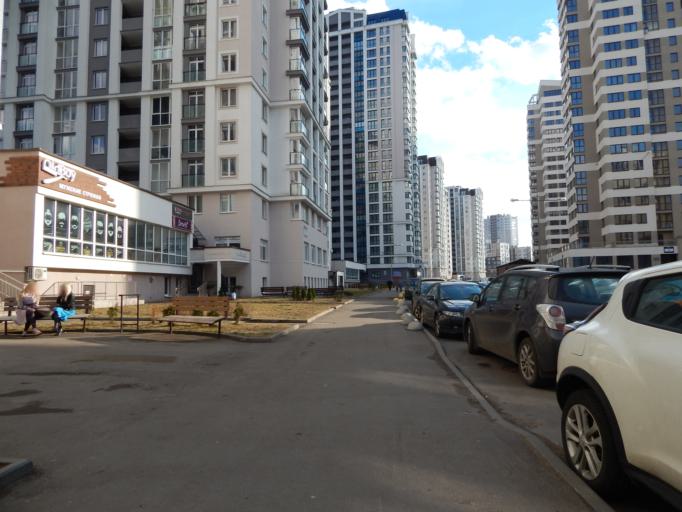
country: BY
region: Minsk
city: Borovlyany
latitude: 53.9325
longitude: 27.6545
